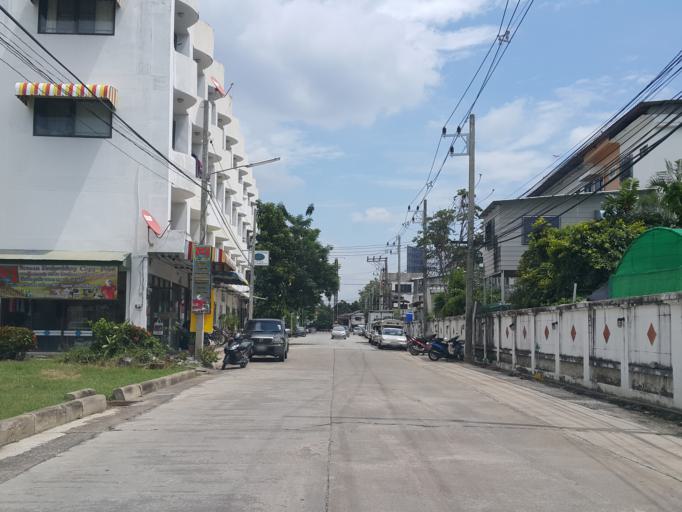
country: TH
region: Chiang Mai
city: Hang Dong
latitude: 18.7361
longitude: 98.9519
